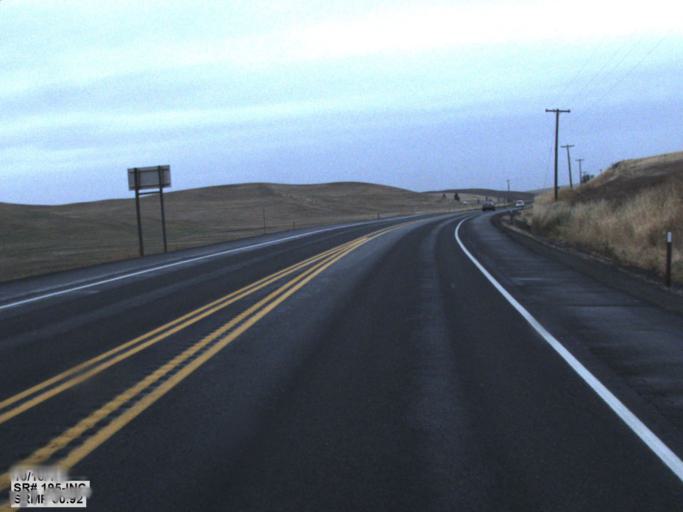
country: US
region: Washington
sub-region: Whitman County
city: Colfax
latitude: 46.7957
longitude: -117.3138
